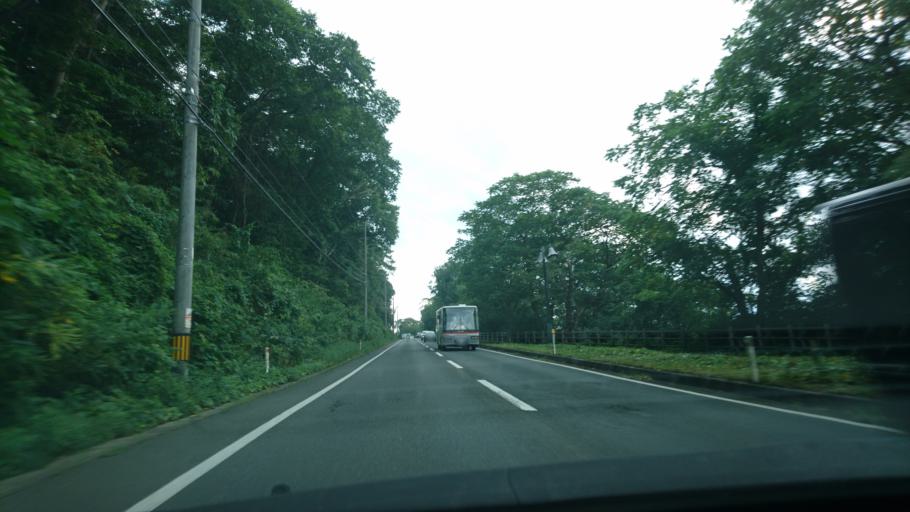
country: JP
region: Iwate
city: Kitakami
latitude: 39.2656
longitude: 141.1259
